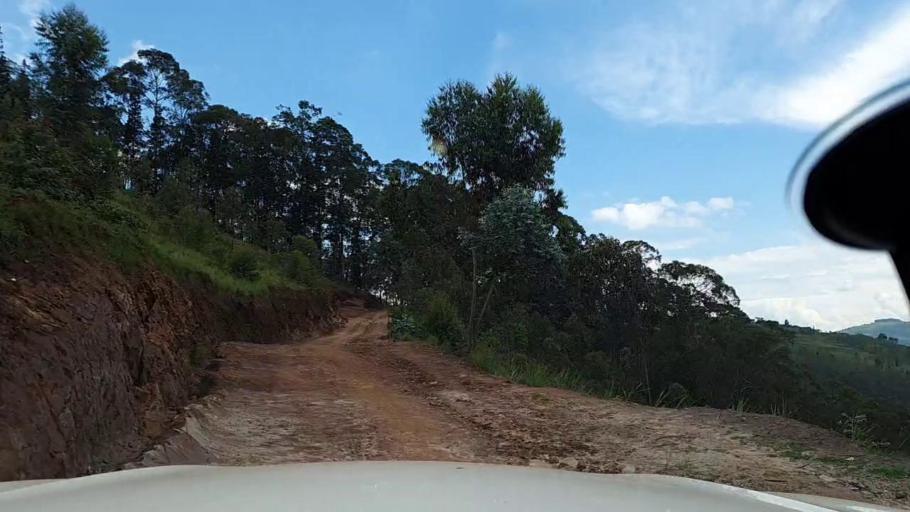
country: RW
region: Southern Province
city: Gitarama
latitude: -1.8083
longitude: 29.8013
